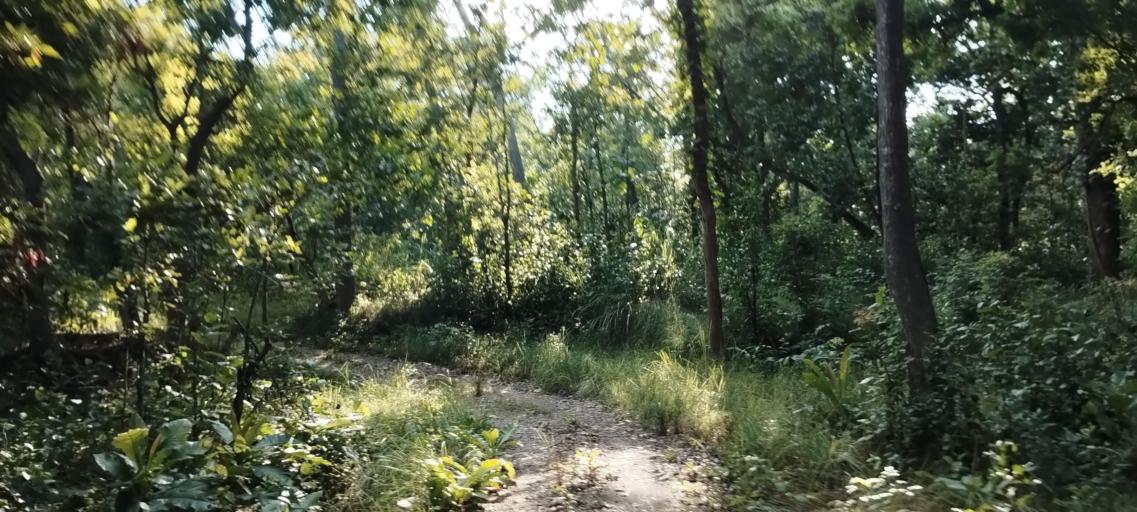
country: NP
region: Far Western
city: Tikapur
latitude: 28.5189
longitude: 81.2753
